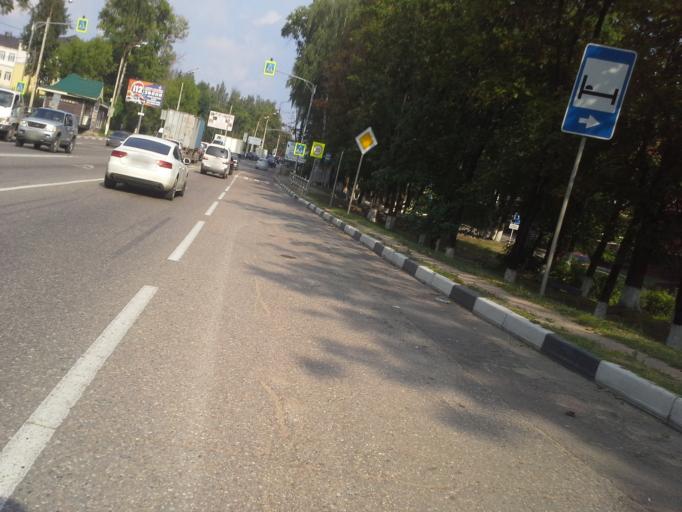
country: RU
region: Moskovskaya
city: Istra
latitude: 55.9208
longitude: 36.8552
